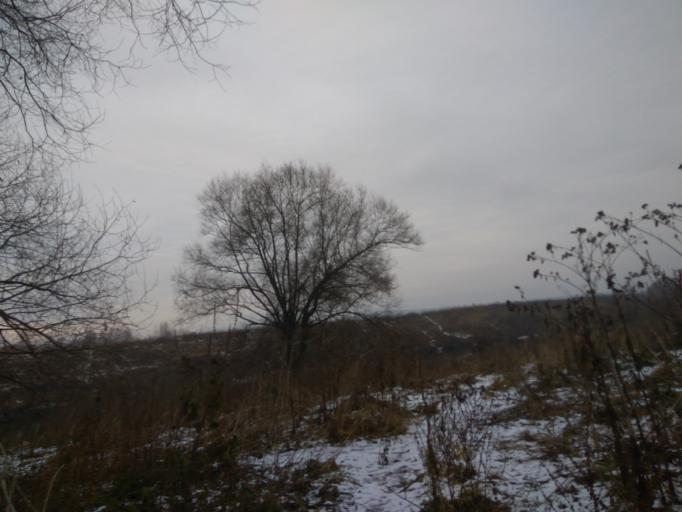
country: RU
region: Moskovskaya
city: Gorki-Leninskiye
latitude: 55.4763
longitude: 37.8035
